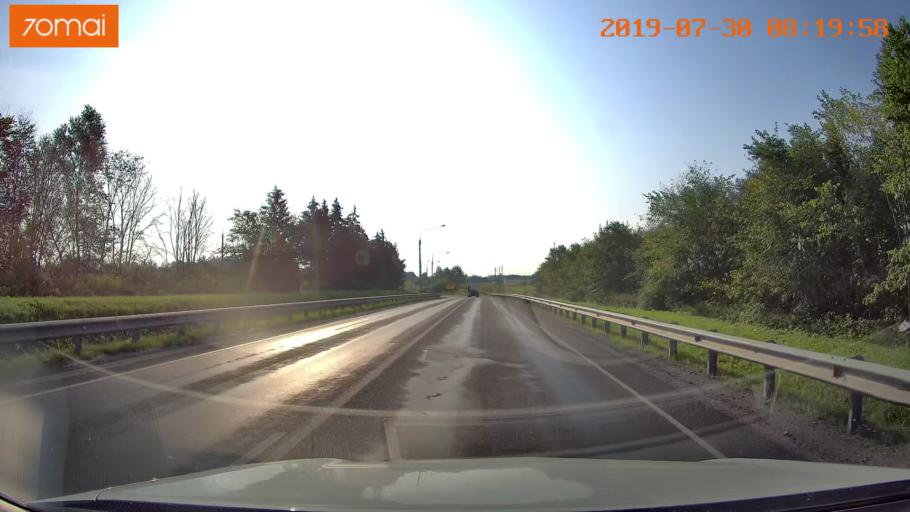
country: RU
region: Kaliningrad
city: Chernyakhovsk
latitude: 54.6261
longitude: 21.5055
